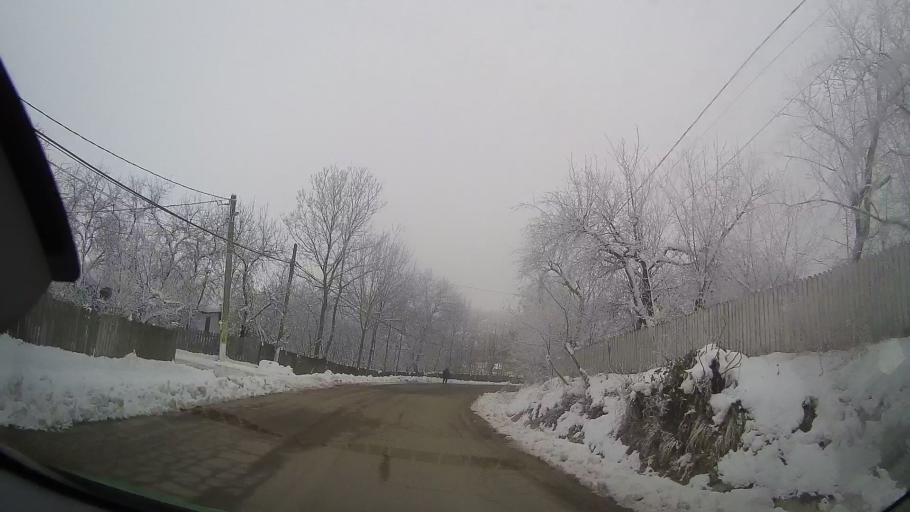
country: RO
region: Iasi
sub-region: Comuna Tansa
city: Tansa
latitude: 46.9083
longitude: 27.2403
